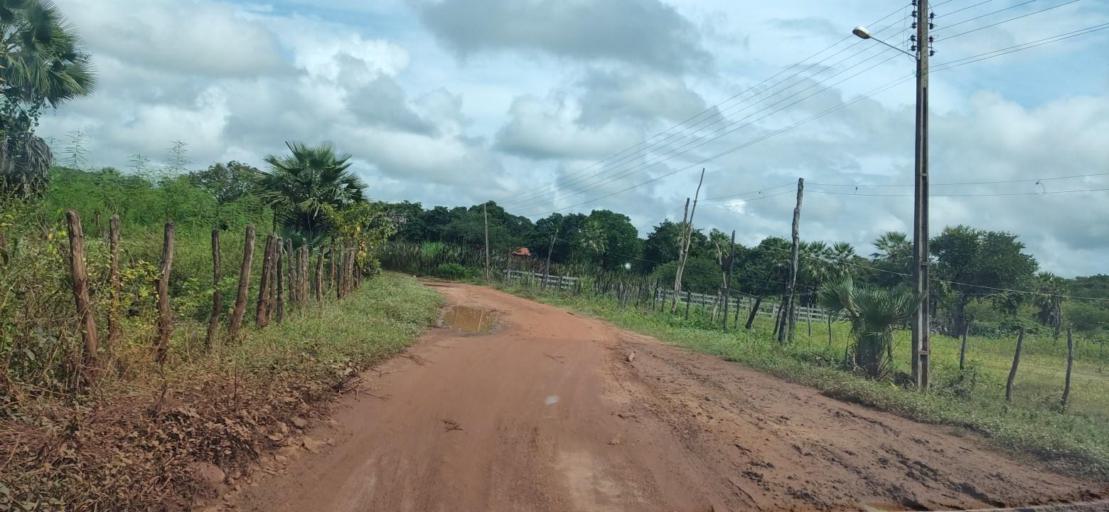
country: BR
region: Piaui
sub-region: Valenca Do Piaui
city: Valenca do Piaui
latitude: -6.1097
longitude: -41.8011
